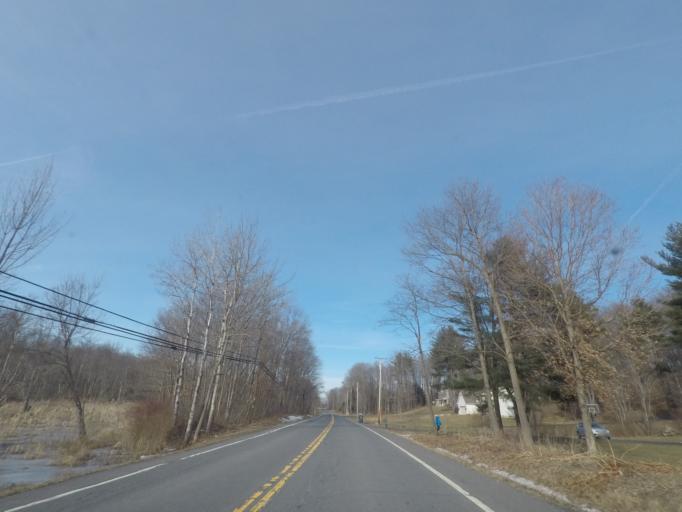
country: US
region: New York
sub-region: Rensselaer County
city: Nassau
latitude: 42.4819
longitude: -73.6246
